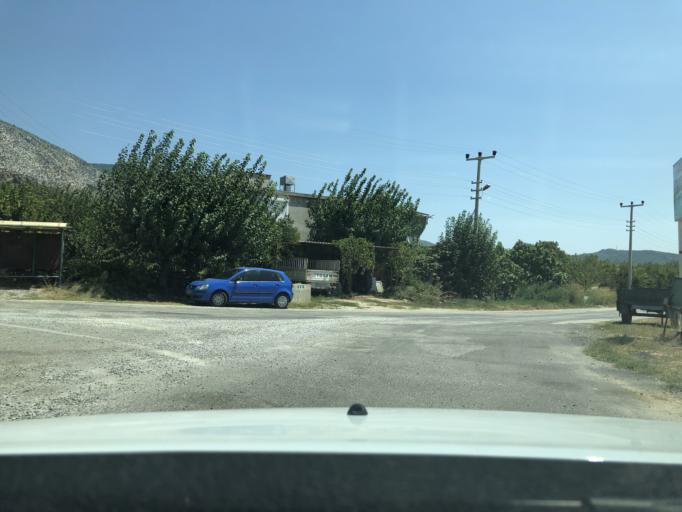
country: TR
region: Antalya
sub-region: Manavgat
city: Kizilagac
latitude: 36.8573
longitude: 31.5628
